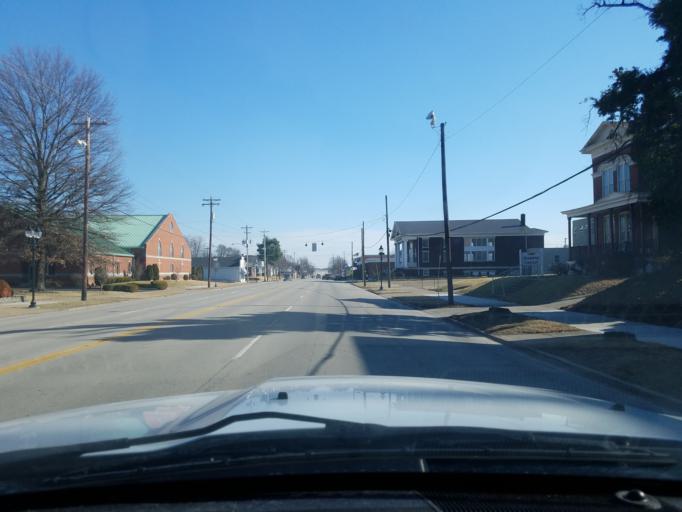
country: US
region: Kentucky
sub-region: Henderson County
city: Henderson
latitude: 37.8389
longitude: -87.5868
